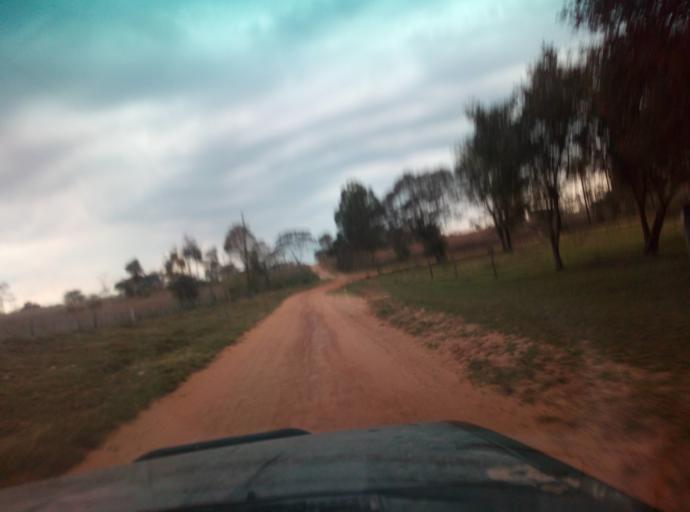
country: PY
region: Caaguazu
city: Doctor Cecilio Baez
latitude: -25.1411
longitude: -56.2239
